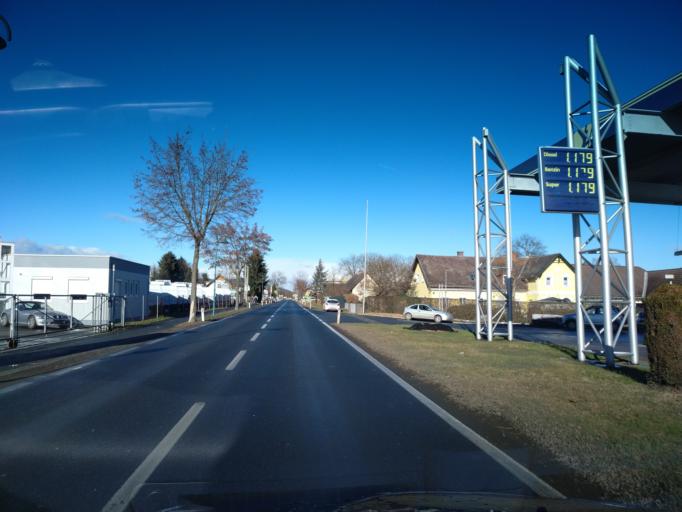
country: AT
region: Styria
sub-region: Politischer Bezirk Leibnitz
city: Kaindorf an der Sulm
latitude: 46.8144
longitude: 15.5485
